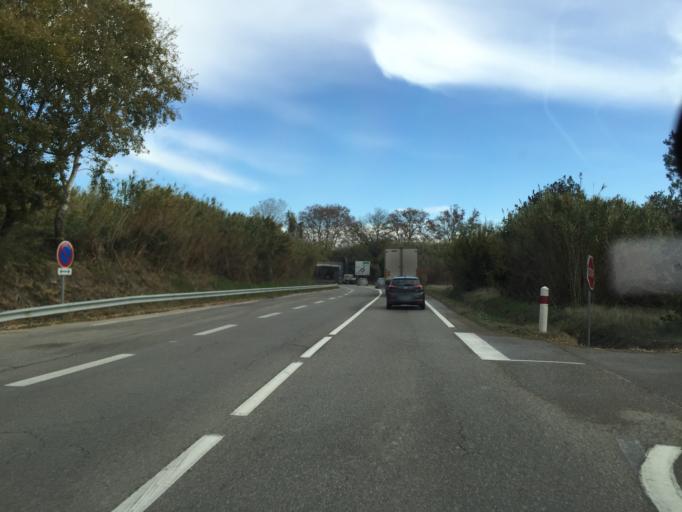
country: FR
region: Provence-Alpes-Cote d'Azur
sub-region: Departement du Vaucluse
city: Lagnes
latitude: 43.8707
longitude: 5.1109
